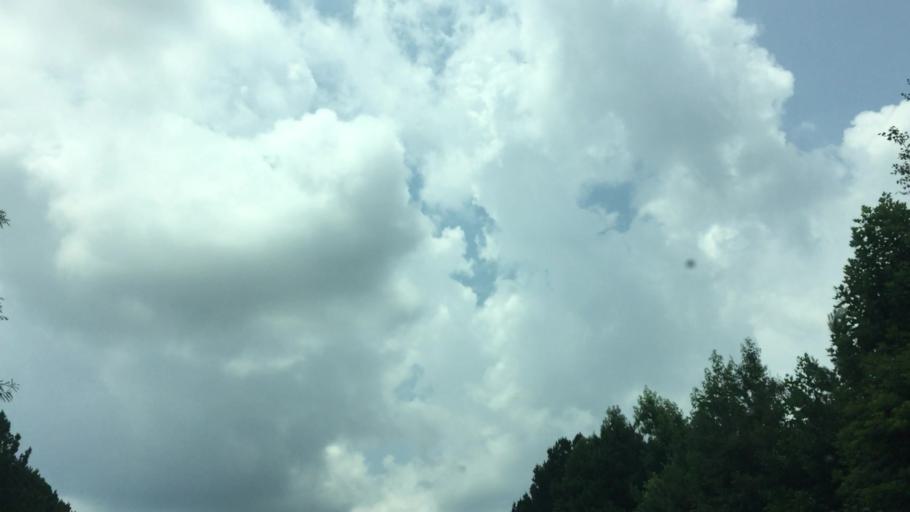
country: US
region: Georgia
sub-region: Fulton County
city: Fairburn
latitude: 33.6109
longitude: -84.6087
